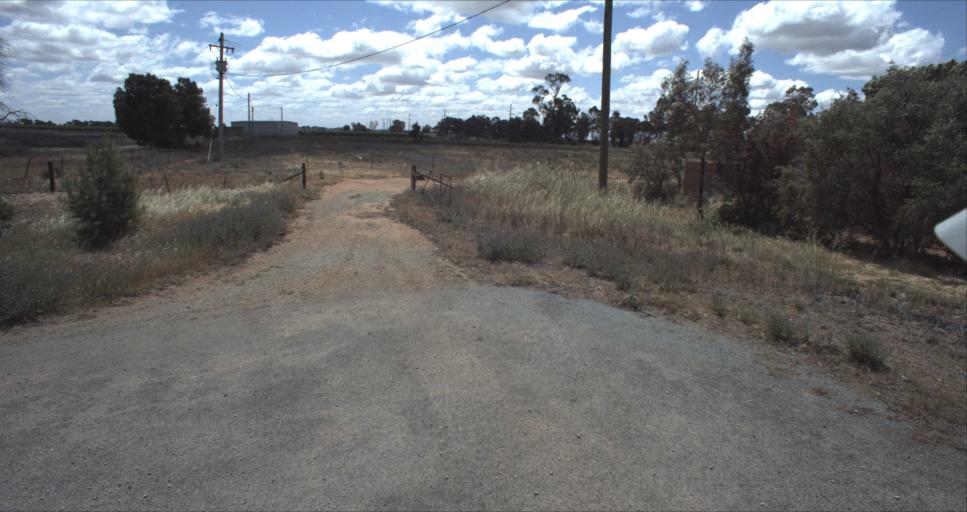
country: AU
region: New South Wales
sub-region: Murrumbidgee Shire
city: Darlington Point
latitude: -34.5104
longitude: 146.1849
